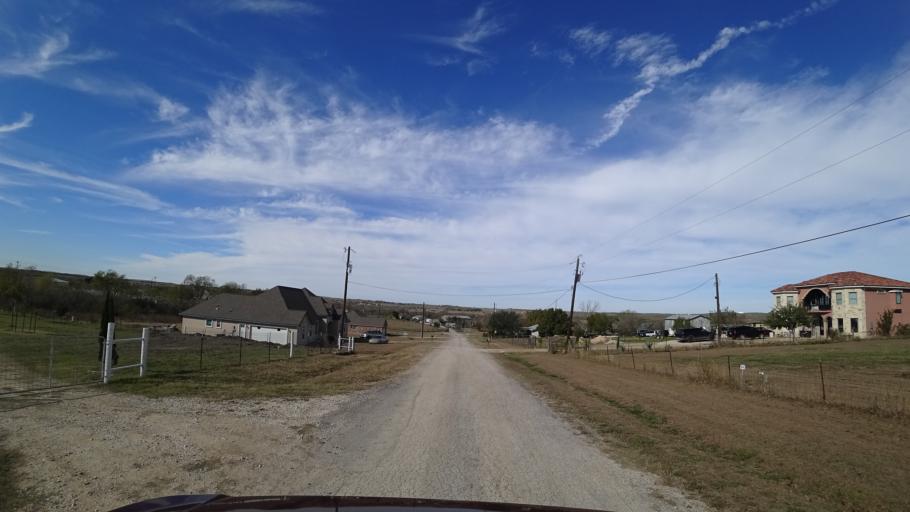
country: US
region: Texas
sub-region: Travis County
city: Onion Creek
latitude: 30.1261
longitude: -97.6926
